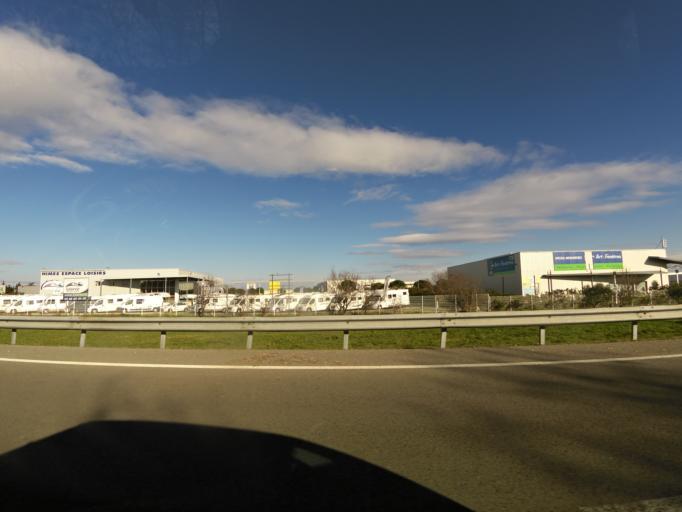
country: FR
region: Languedoc-Roussillon
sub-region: Departement du Gard
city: Milhaud
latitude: 43.7953
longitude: 4.3183
